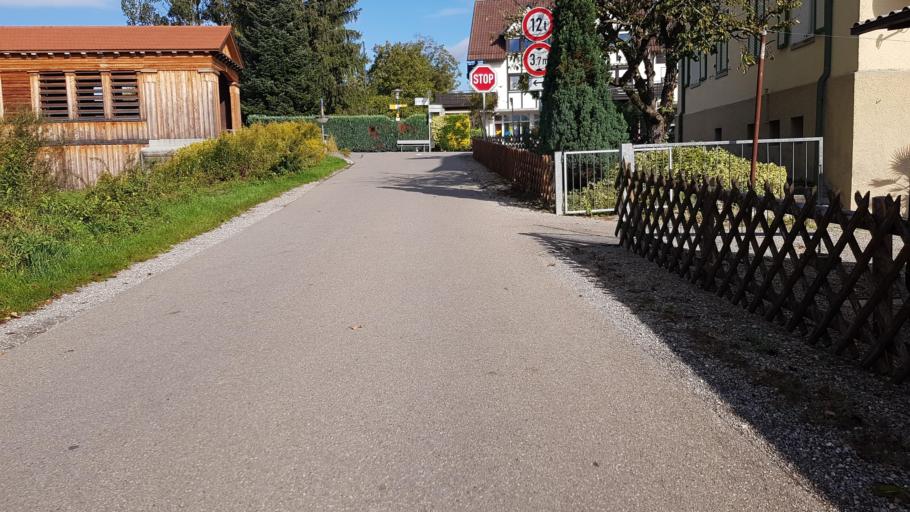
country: DE
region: Baden-Wuerttemberg
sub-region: Tuebingen Region
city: Eriskirch
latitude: 47.6280
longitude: 9.5323
